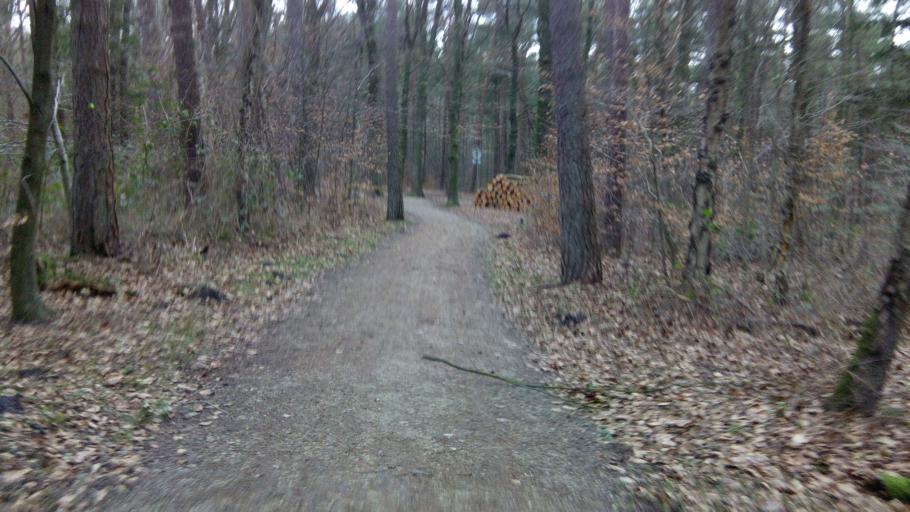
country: NL
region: North Holland
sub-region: Gemeente Hilversum
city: Hilversum
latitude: 52.1875
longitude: 5.2250
